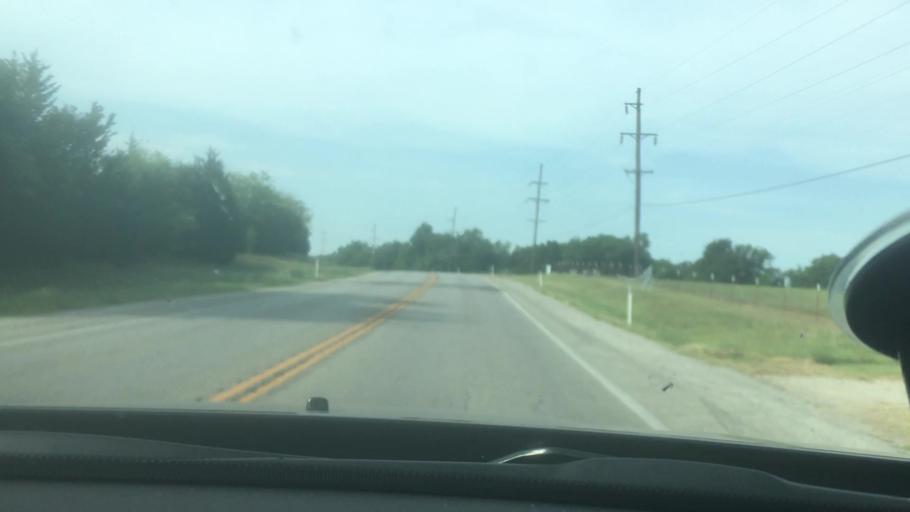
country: US
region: Oklahoma
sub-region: Carter County
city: Ardmore
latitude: 34.1222
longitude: -97.1434
